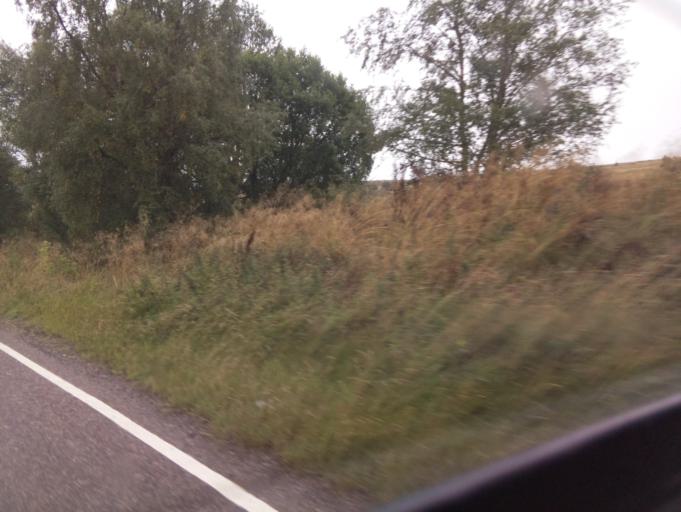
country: GB
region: Scotland
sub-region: Highland
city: Grantown on Spey
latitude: 57.2372
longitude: -3.3521
